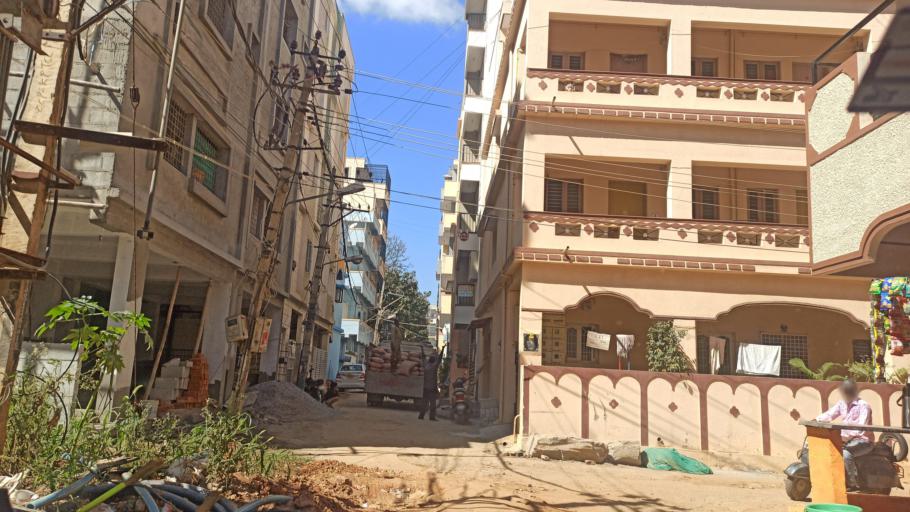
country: IN
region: Karnataka
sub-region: Bangalore Urban
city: Bangalore
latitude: 12.9281
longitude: 77.6749
